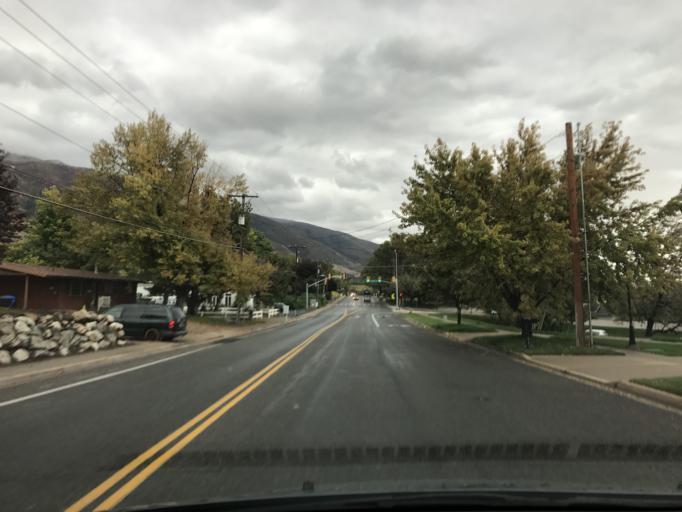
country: US
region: Utah
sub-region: Davis County
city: Farmington
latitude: 41.0018
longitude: -111.9015
